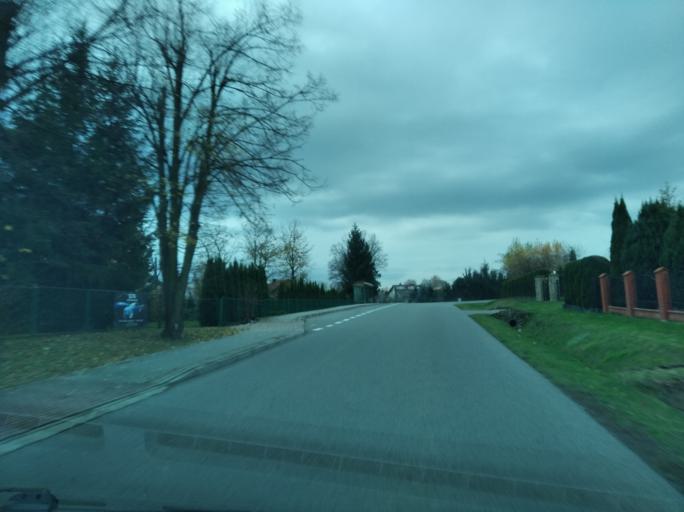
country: PL
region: Subcarpathian Voivodeship
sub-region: Powiat ropczycko-sedziszowski
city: Iwierzyce
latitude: 49.9905
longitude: 21.7282
